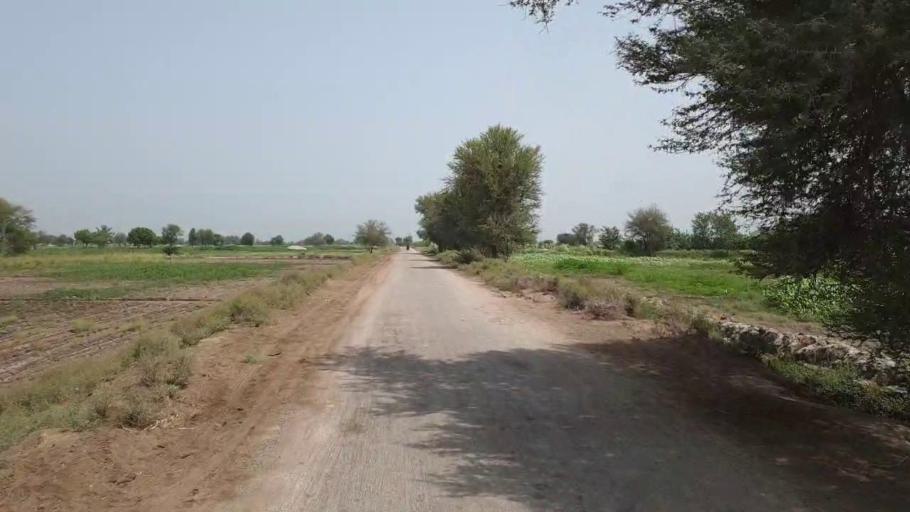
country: PK
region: Sindh
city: Nawabshah
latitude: 26.2637
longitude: 68.3179
